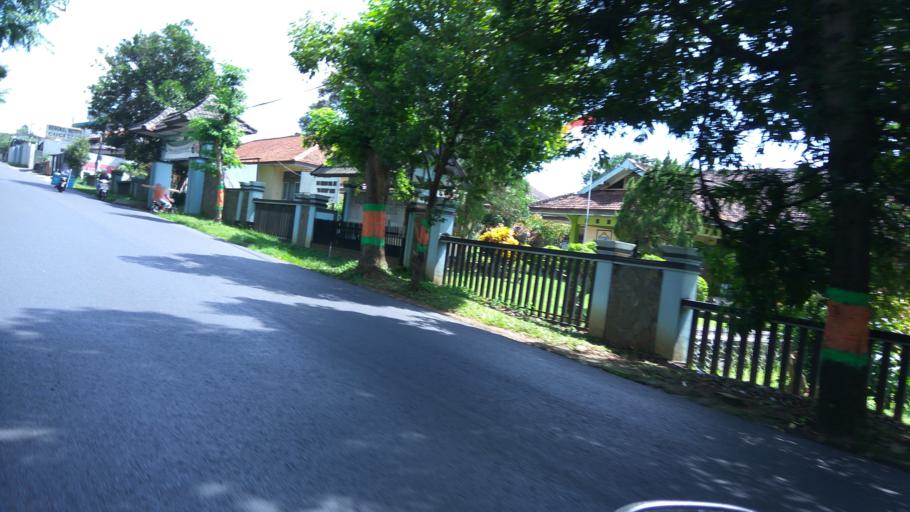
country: ID
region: Central Java
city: Ungaran
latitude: -7.1157
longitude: 110.4080
